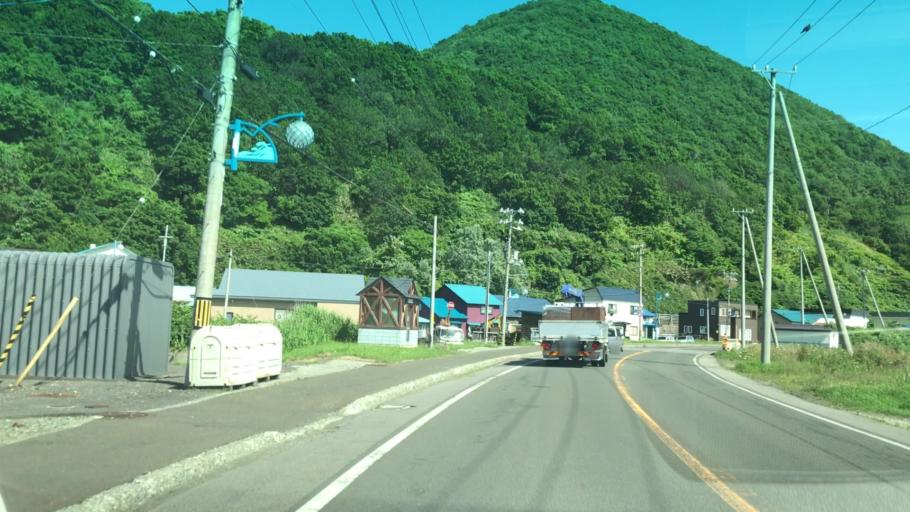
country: JP
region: Hokkaido
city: Iwanai
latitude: 43.1062
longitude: 140.4582
